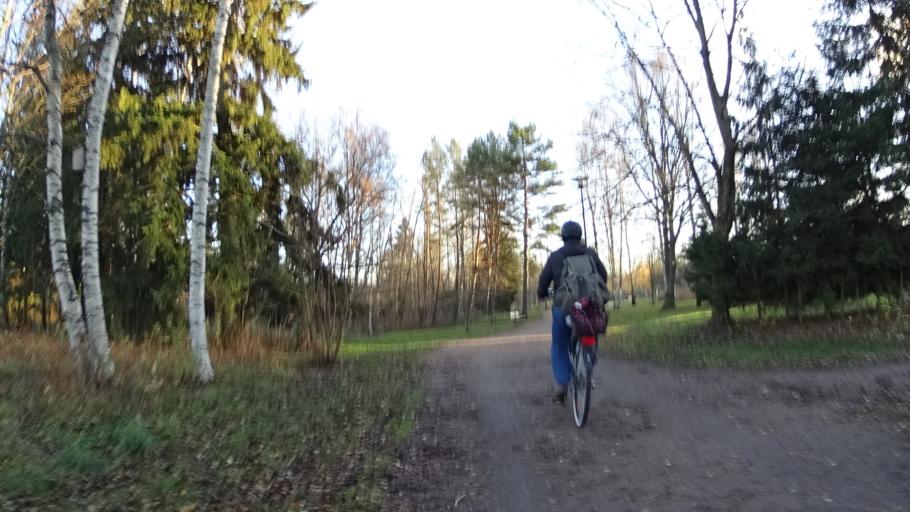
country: FI
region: Uusimaa
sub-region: Helsinki
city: Vantaa
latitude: 60.2958
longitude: 25.0138
